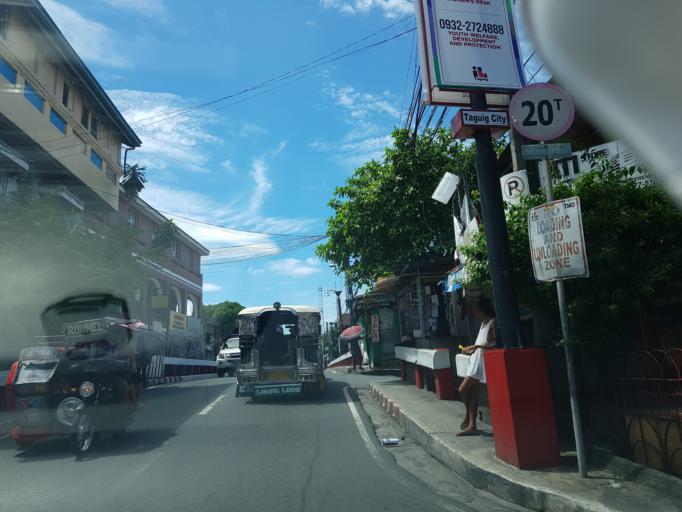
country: PH
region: Calabarzon
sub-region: Province of Rizal
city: Taguig
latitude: 14.5284
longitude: 121.0714
